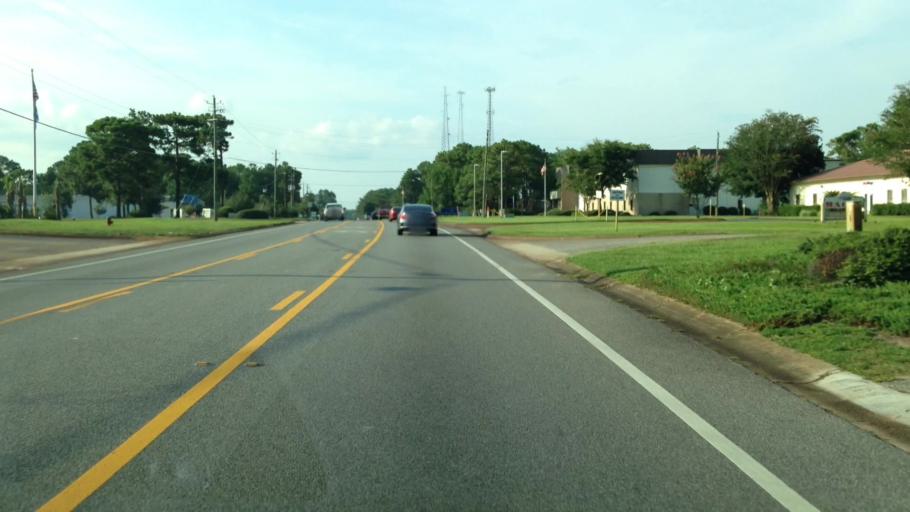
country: US
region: Florida
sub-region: Okaloosa County
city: Mary Esther
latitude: 30.4182
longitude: -86.6674
